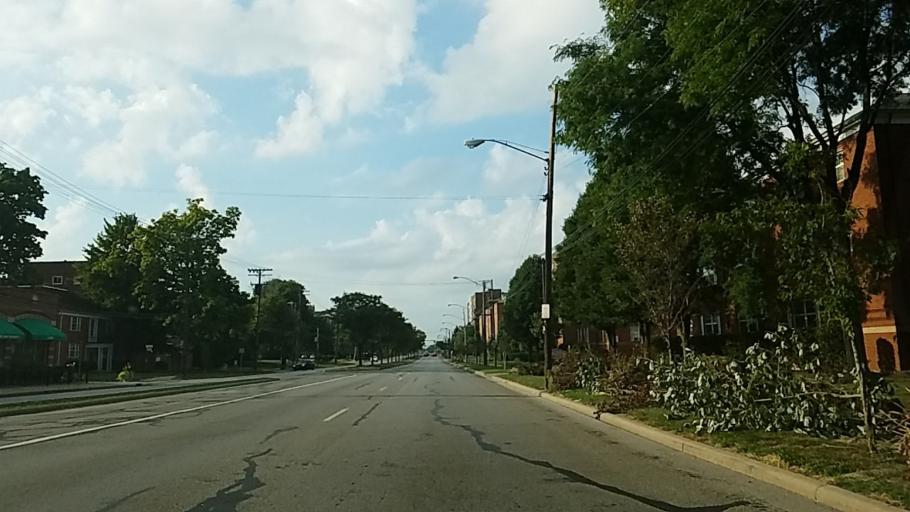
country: US
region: Ohio
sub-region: Cuyahoga County
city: Shaker Heights
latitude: 41.4720
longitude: -81.5364
